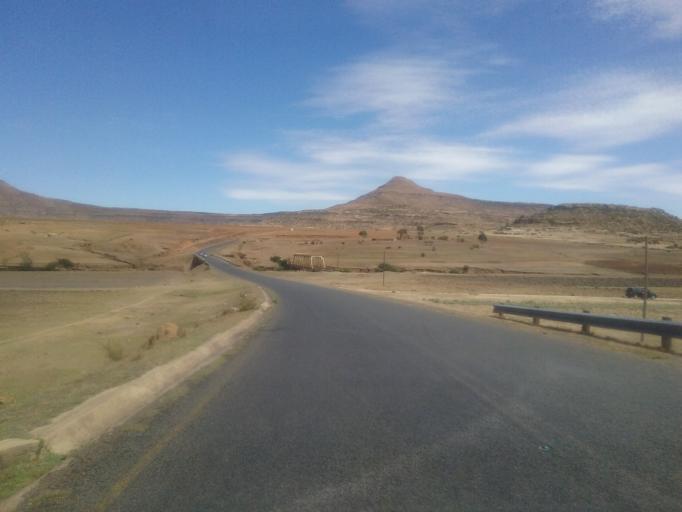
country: LS
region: Mohale's Hoek District
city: Mohale's Hoek
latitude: -30.0912
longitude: 27.4362
